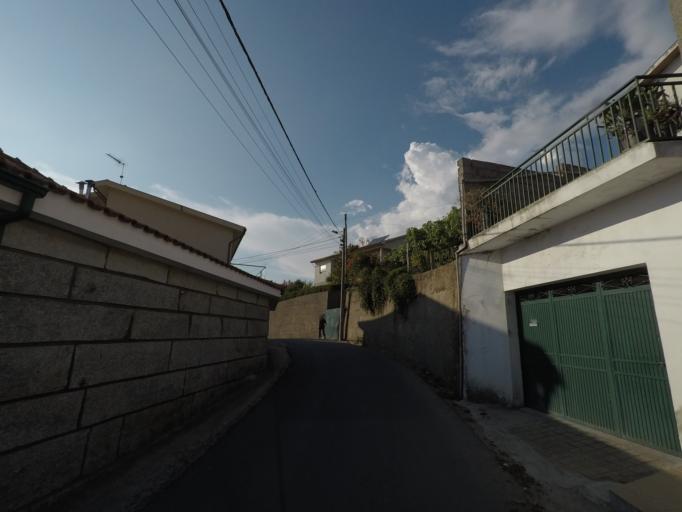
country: PT
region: Vila Real
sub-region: Mesao Frio
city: Mesao Frio
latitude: 41.1662
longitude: -7.9250
